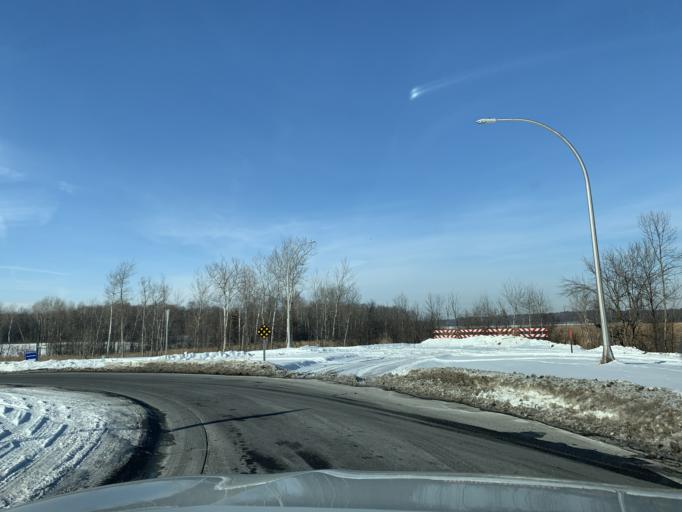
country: US
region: Minnesota
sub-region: Anoka County
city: Columbus
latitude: 45.2505
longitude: -93.0296
